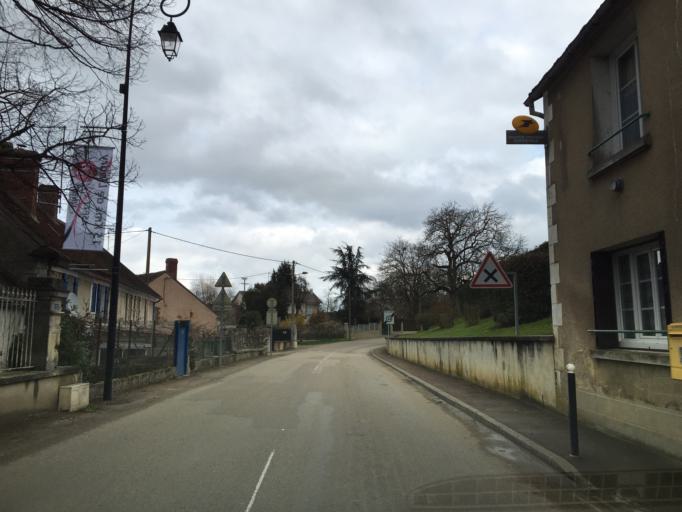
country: FR
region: Bourgogne
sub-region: Departement de l'Yonne
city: Pourrain
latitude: 47.8007
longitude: 3.4206
